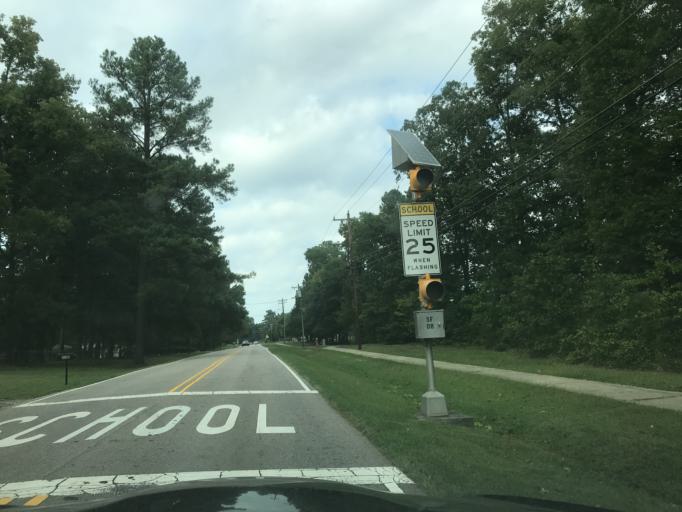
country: US
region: North Carolina
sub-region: Durham County
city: Durham
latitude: 35.9303
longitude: -78.9101
